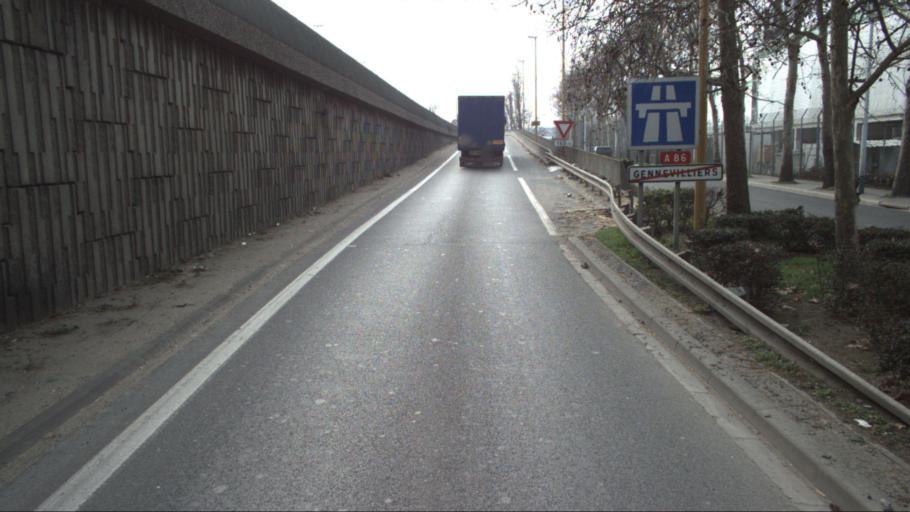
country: FR
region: Ile-de-France
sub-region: Departement des Hauts-de-Seine
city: Villeneuve-la-Garenne
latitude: 48.9337
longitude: 2.3207
